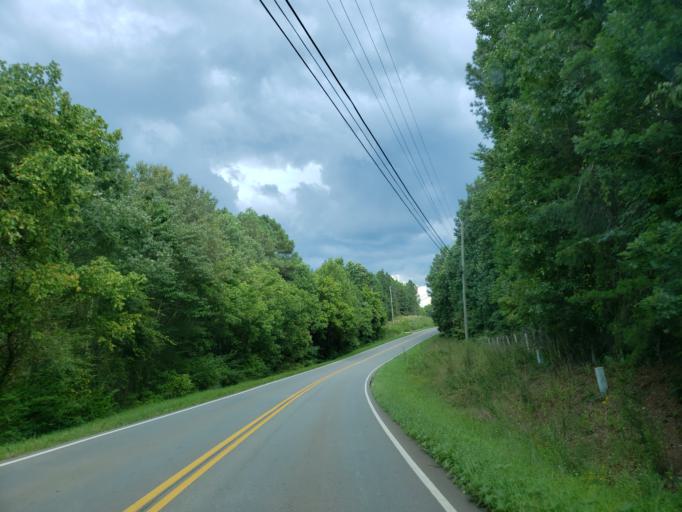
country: US
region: Georgia
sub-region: Pickens County
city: Jasper
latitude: 34.3991
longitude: -84.4718
